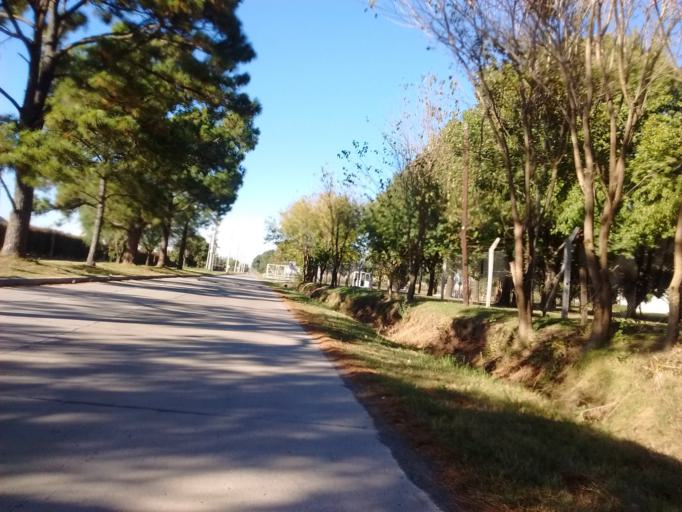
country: AR
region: Santa Fe
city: Funes
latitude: -32.9335
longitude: -60.8120
